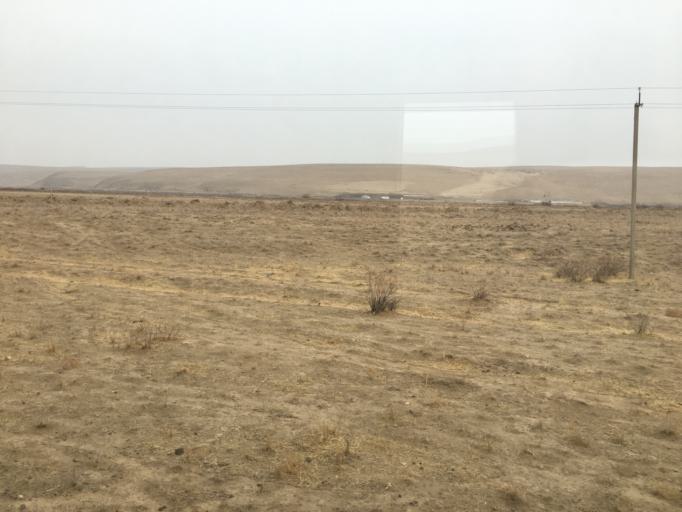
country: TM
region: Mary
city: Serhetabat
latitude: 35.5579
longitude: 62.5189
